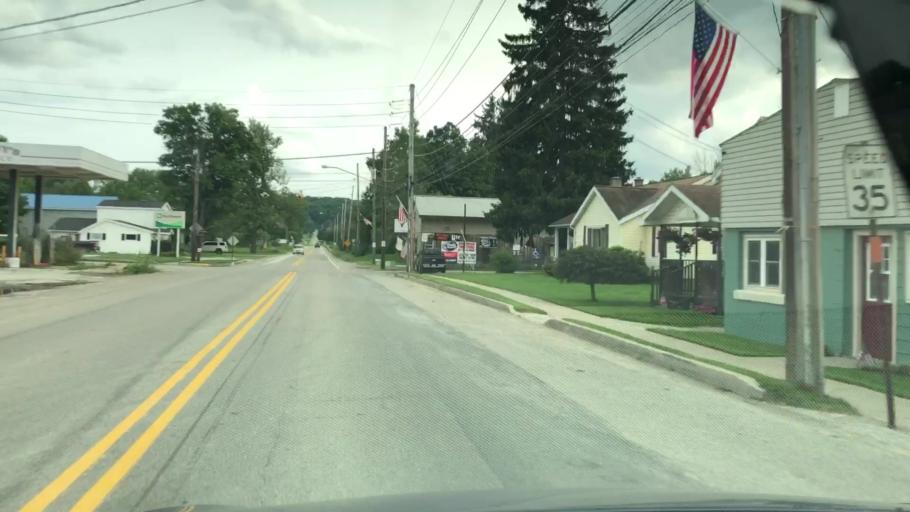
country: US
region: Pennsylvania
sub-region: Erie County
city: Union City
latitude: 42.0013
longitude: -79.8109
